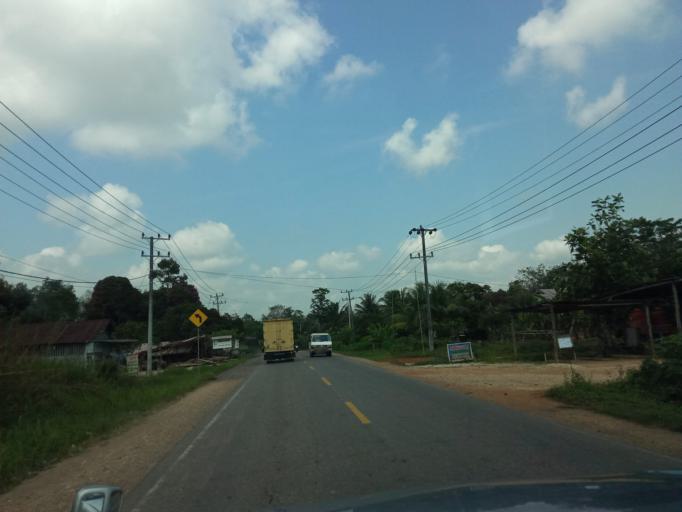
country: ID
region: Jambi
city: Muara Bulian
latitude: -1.7348
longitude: 103.2083
